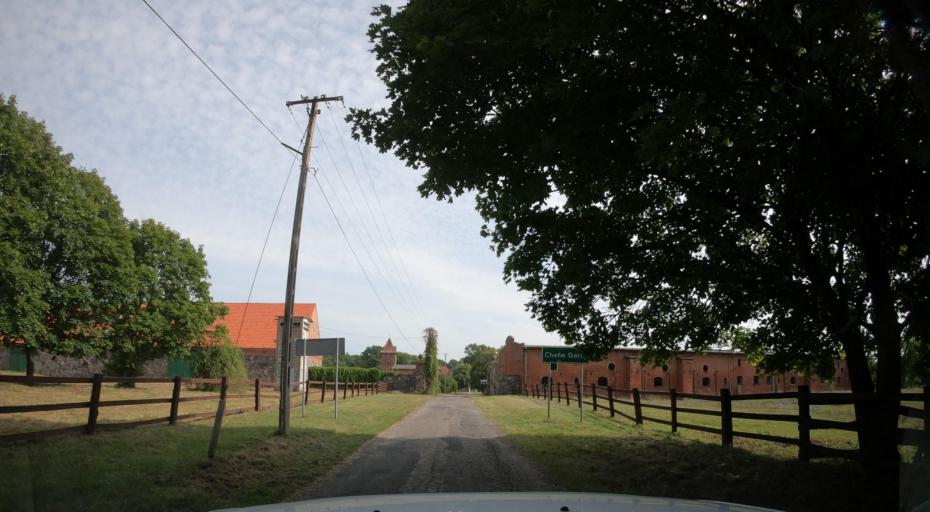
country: PL
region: West Pomeranian Voivodeship
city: Trzcinsko Zdroj
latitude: 52.8804
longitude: 14.5843
